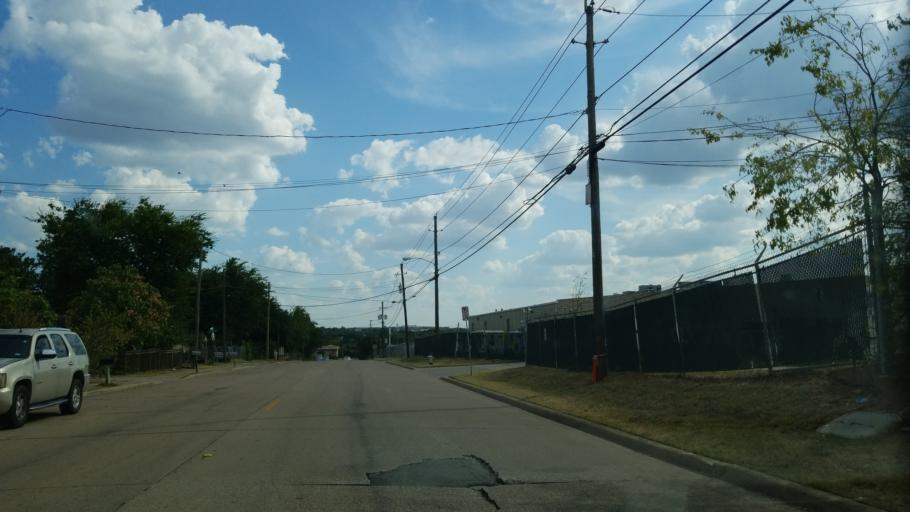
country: US
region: Texas
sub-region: Dallas County
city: Dallas
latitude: 32.7680
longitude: -96.8480
